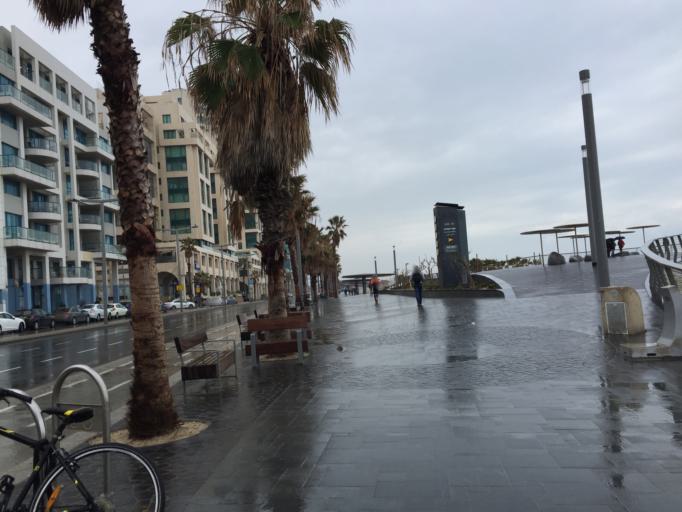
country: IL
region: Tel Aviv
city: Tel Aviv
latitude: 32.0732
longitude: 34.7647
